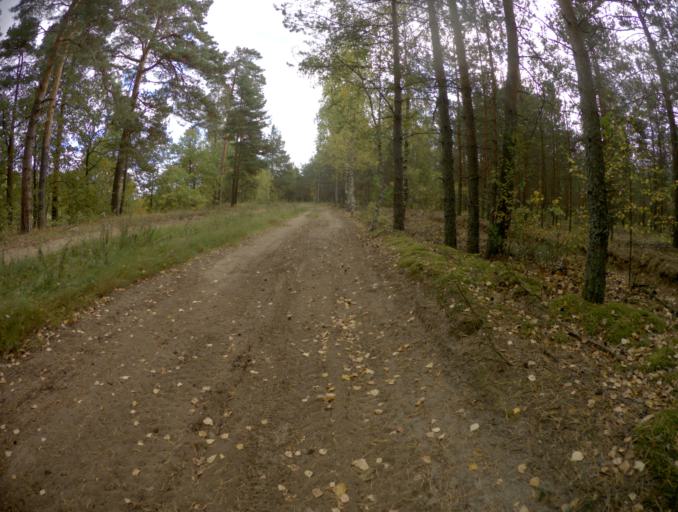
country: RU
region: Vladimir
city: Petushki
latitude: 55.8850
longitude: 39.5018
